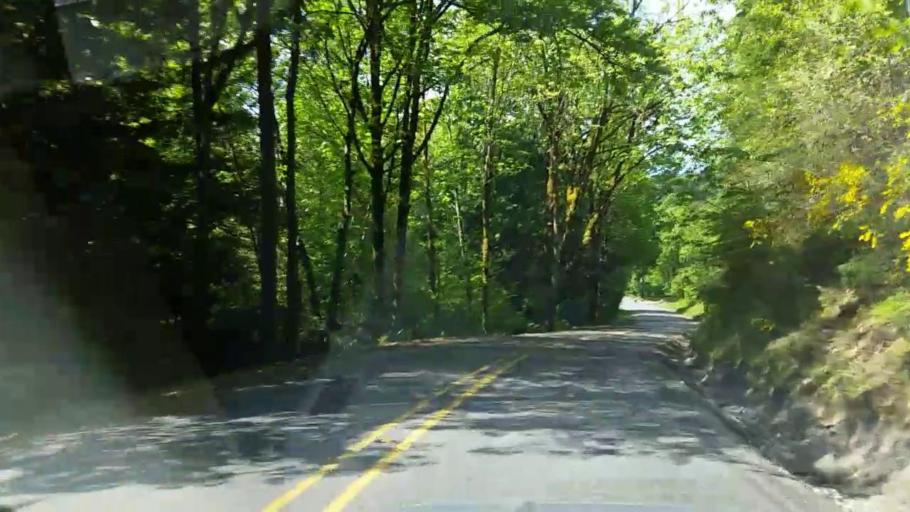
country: US
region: Washington
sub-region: Pierce County
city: Key Center
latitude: 47.3390
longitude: -122.7591
